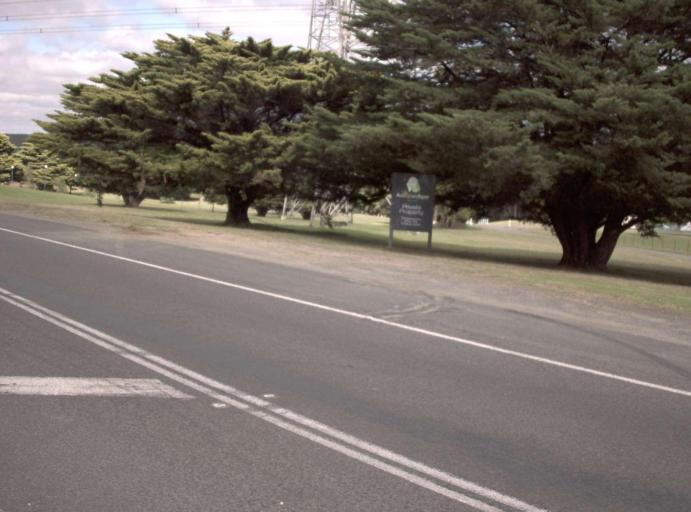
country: AU
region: Victoria
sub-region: Latrobe
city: Morwell
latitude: -38.1874
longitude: 146.4532
